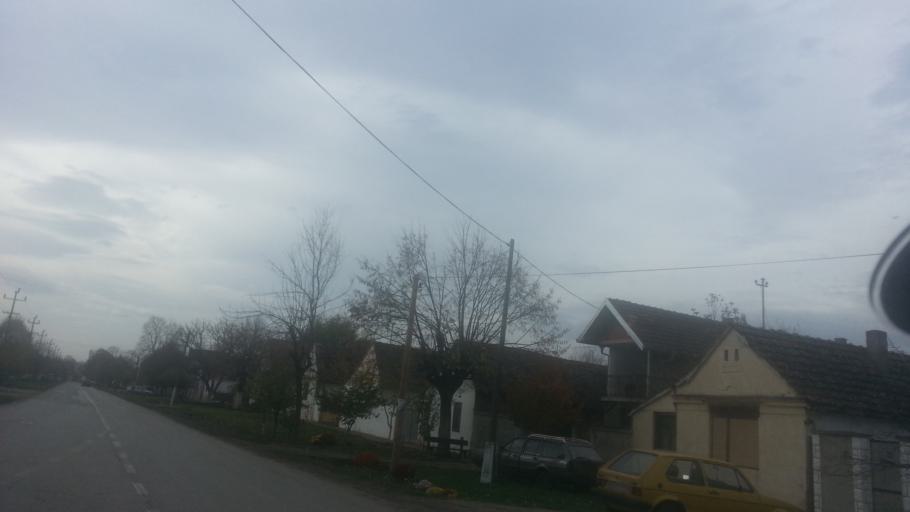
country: RS
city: Putinci
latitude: 44.9916
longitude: 19.9826
